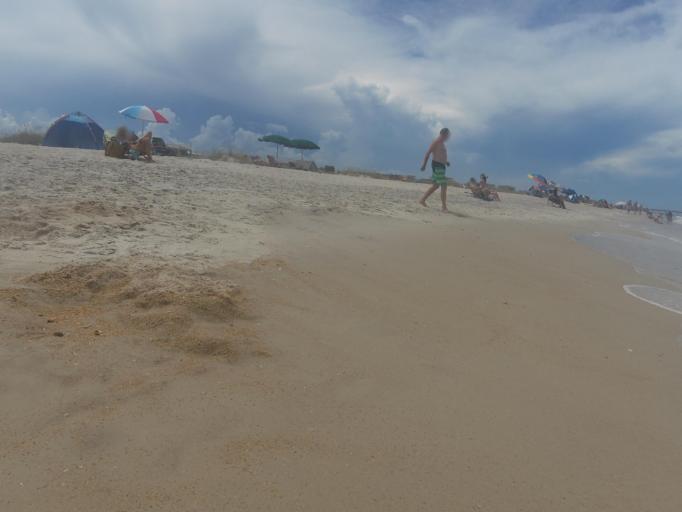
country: US
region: Florida
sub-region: Saint Johns County
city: Saint Augustine Beach
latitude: 29.8467
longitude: -81.2641
